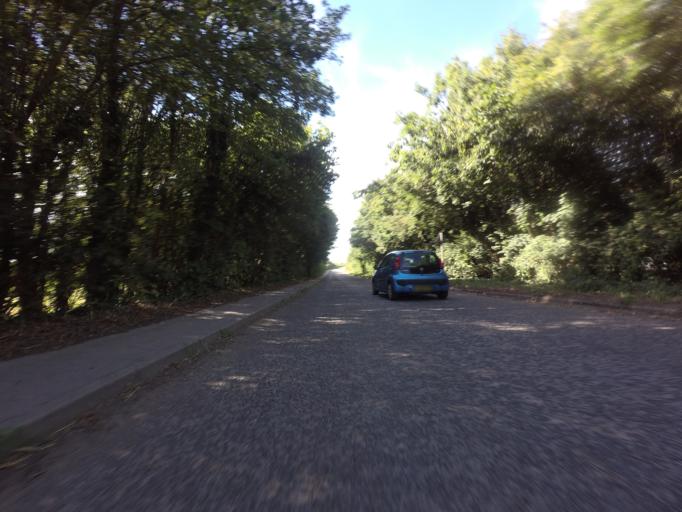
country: GB
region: England
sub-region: Kent
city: Birchington-on-Sea
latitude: 51.3572
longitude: 1.2461
